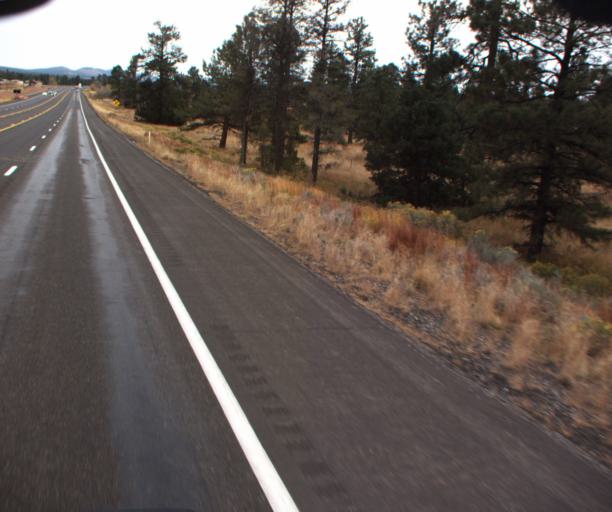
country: US
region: Arizona
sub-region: Coconino County
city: Flagstaff
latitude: 35.3390
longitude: -111.5556
